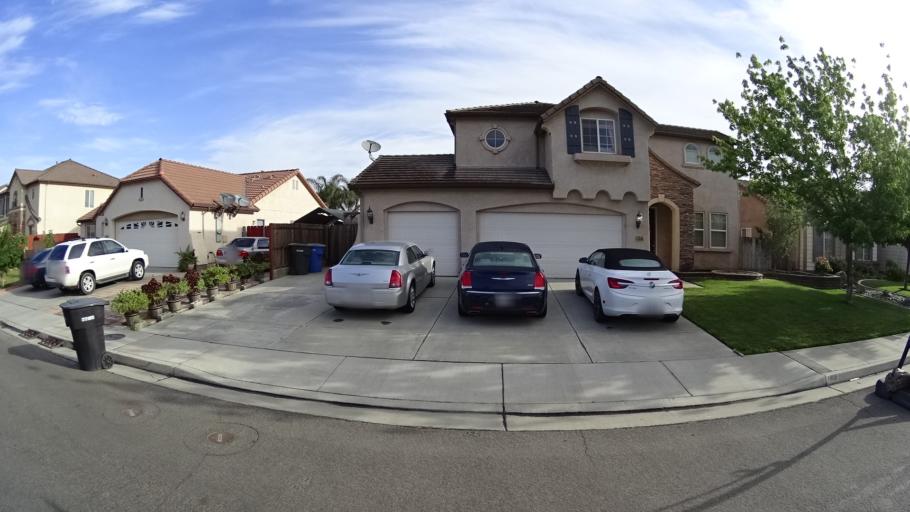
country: US
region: California
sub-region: Kings County
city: Hanford
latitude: 36.3456
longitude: -119.6769
